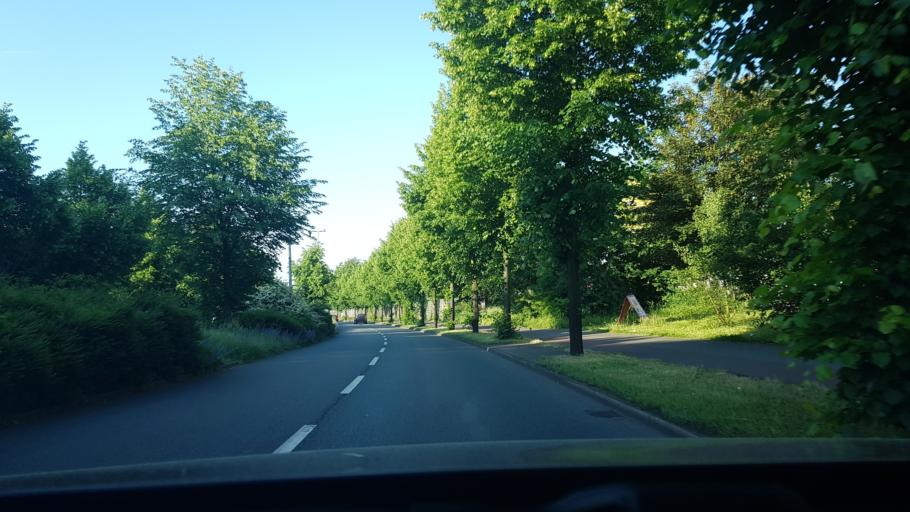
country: DE
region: North Rhine-Westphalia
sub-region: Regierungsbezirk Dusseldorf
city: Hochfeld
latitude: 51.4234
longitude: 6.7478
